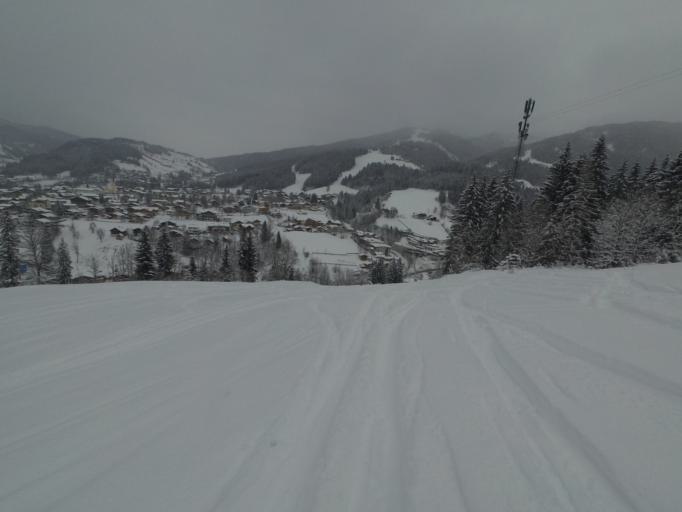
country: AT
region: Salzburg
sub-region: Politischer Bezirk Sankt Johann im Pongau
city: Wagrain
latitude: 47.3282
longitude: 13.2962
